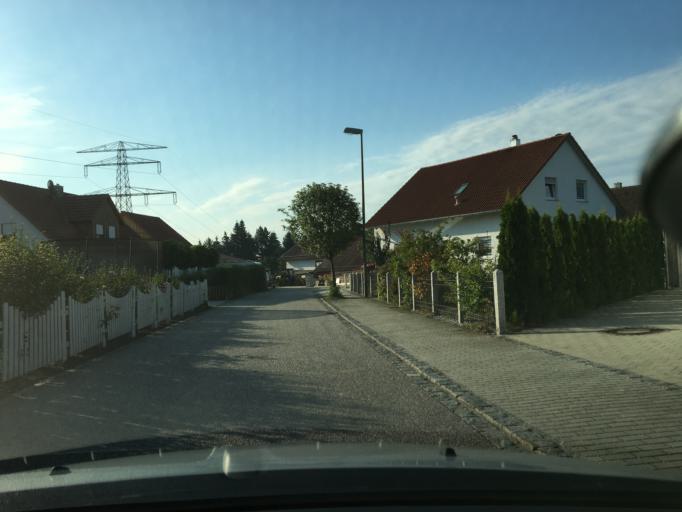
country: DE
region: Bavaria
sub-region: Lower Bavaria
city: Vilsbiburg
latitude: 48.4857
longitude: 12.3404
